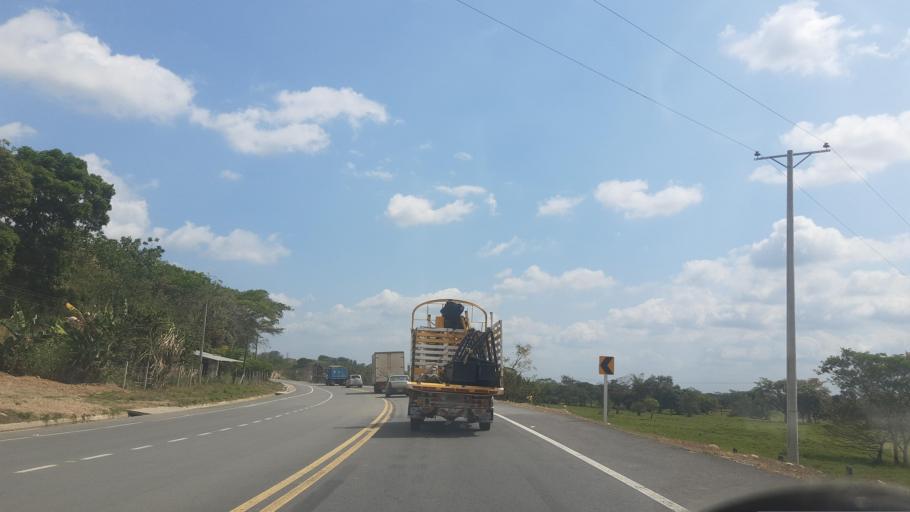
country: CO
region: Casanare
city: Tauramena
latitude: 5.0211
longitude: -72.6616
